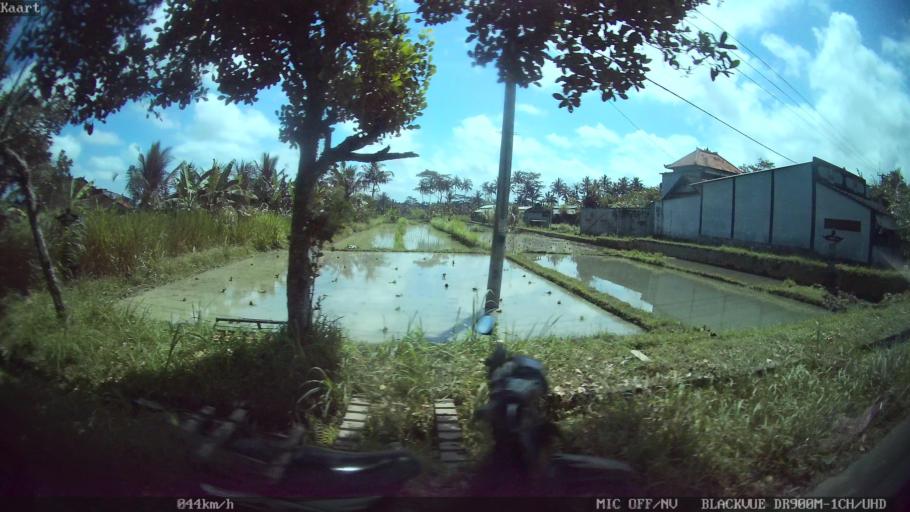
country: ID
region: Bali
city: Banjar Apuan Kaja
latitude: -8.5079
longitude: 115.3374
